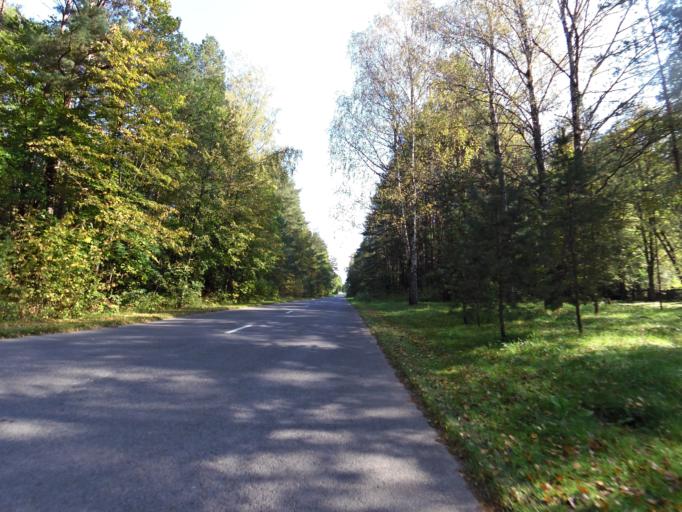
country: LT
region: Vilnius County
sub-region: Vilnius
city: Vilnius
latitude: 54.7430
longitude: 25.2978
